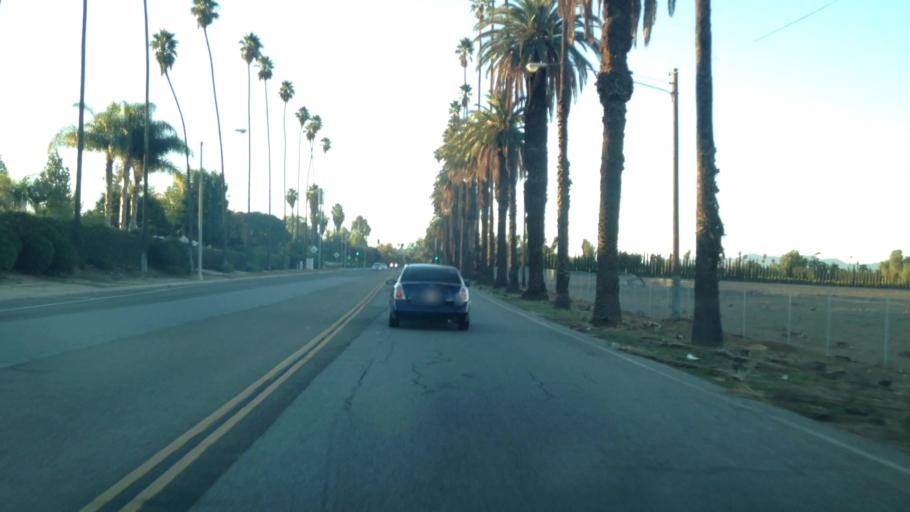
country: US
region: California
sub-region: Riverside County
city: Riverside
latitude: 33.9220
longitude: -117.3835
